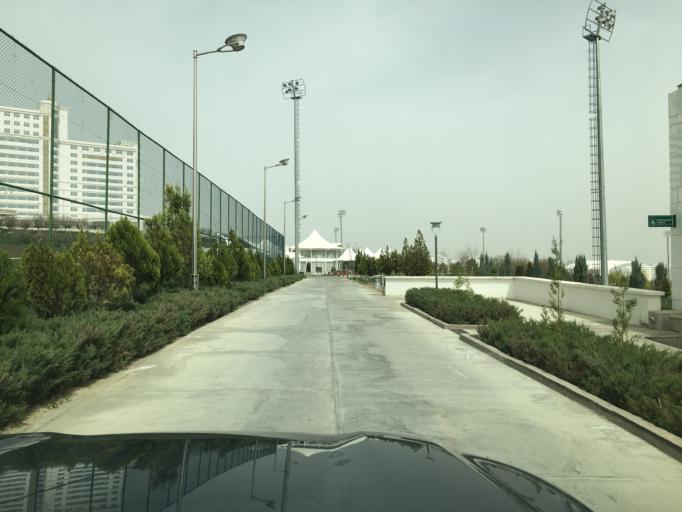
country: TM
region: Ahal
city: Ashgabat
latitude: 37.9270
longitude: 58.3472
